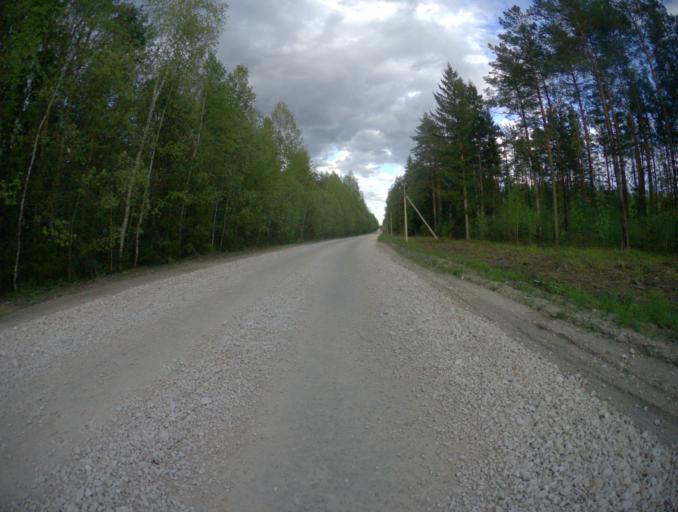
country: RU
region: Vladimir
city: Gusevskiy
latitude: 55.7217
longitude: 40.5748
